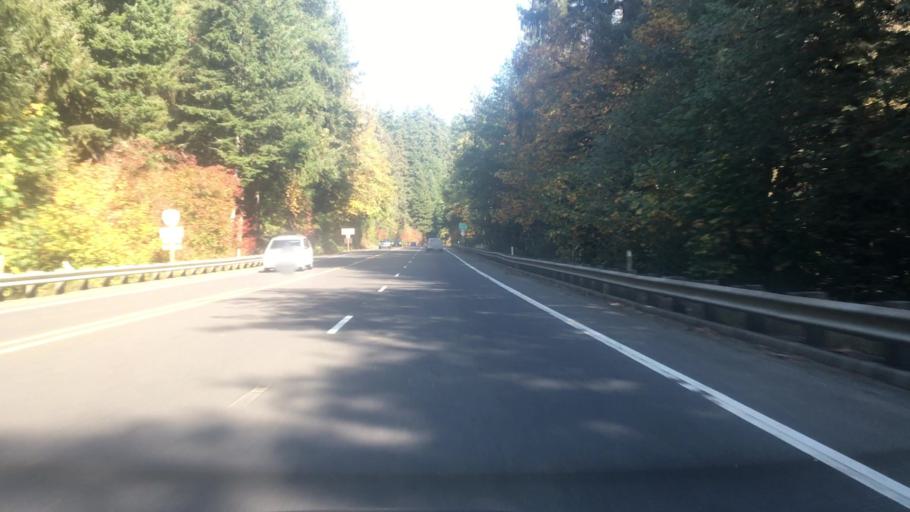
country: US
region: Oregon
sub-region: Lincoln County
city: Rose Lodge
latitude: 45.0439
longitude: -123.8027
